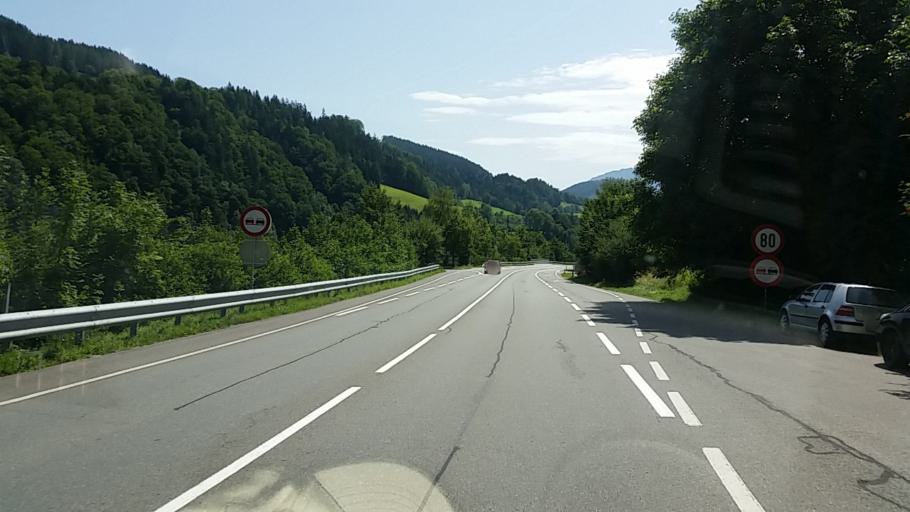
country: AT
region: Salzburg
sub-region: Politischer Bezirk Sankt Johann im Pongau
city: Werfen
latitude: 47.4770
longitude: 13.1899
